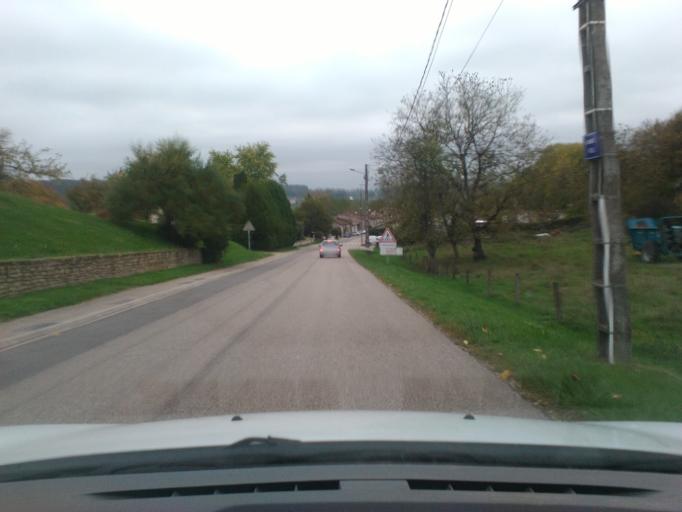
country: FR
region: Lorraine
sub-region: Departement des Vosges
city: Vincey
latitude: 48.3010
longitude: 6.3103
